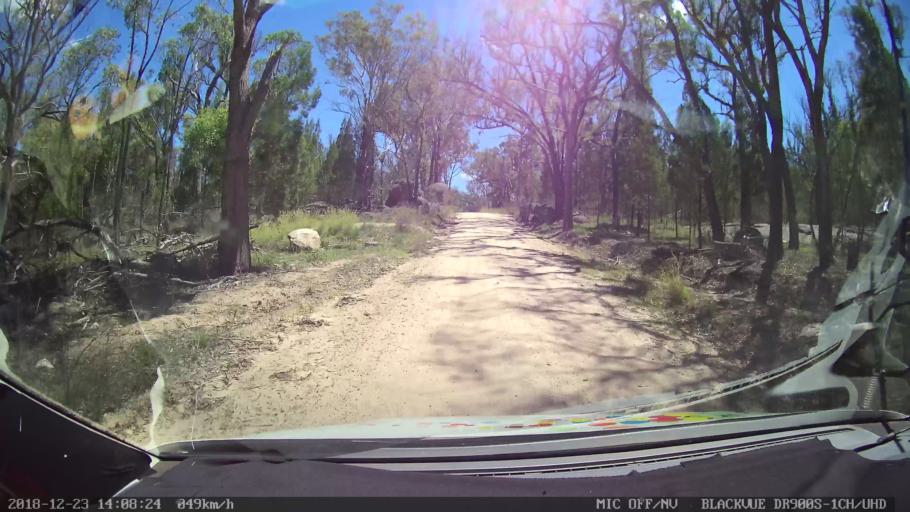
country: AU
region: New South Wales
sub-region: Tamworth Municipality
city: Manilla
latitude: -30.6418
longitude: 151.0681
